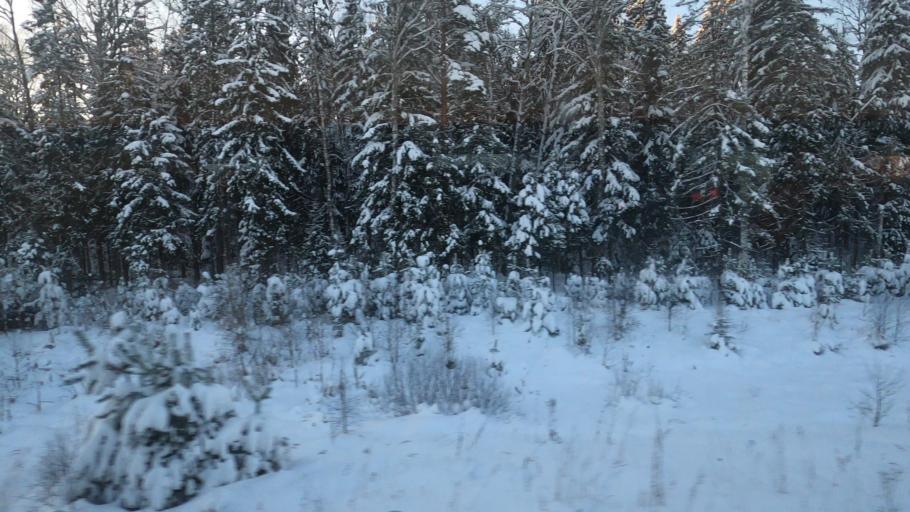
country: RU
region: Moskovskaya
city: Verbilki
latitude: 56.5239
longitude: 37.5580
